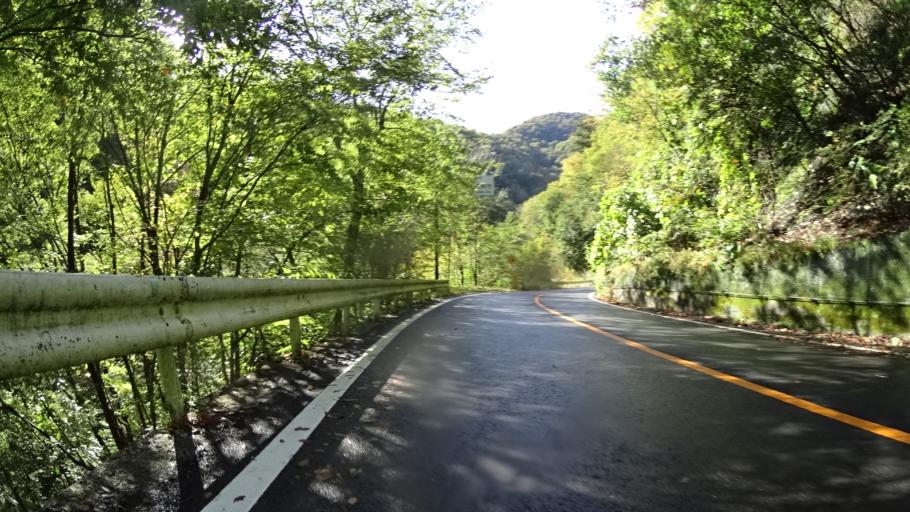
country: JP
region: Yamanashi
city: Enzan
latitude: 35.8048
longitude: 138.8539
